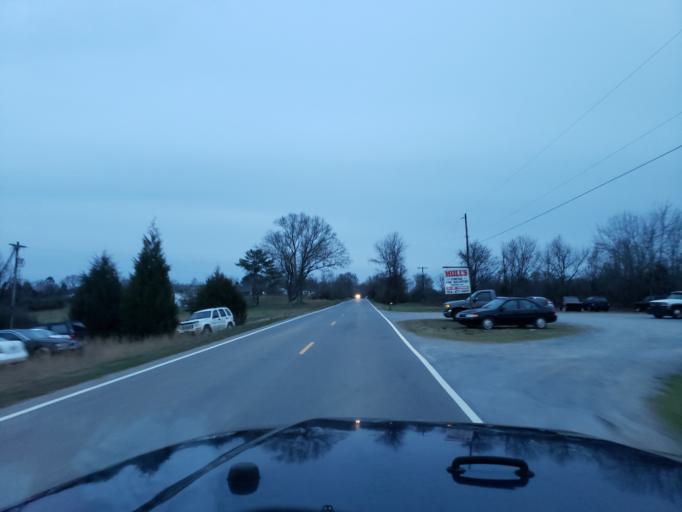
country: US
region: North Carolina
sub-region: Cleveland County
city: White Plains
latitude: 35.2125
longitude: -81.4542
